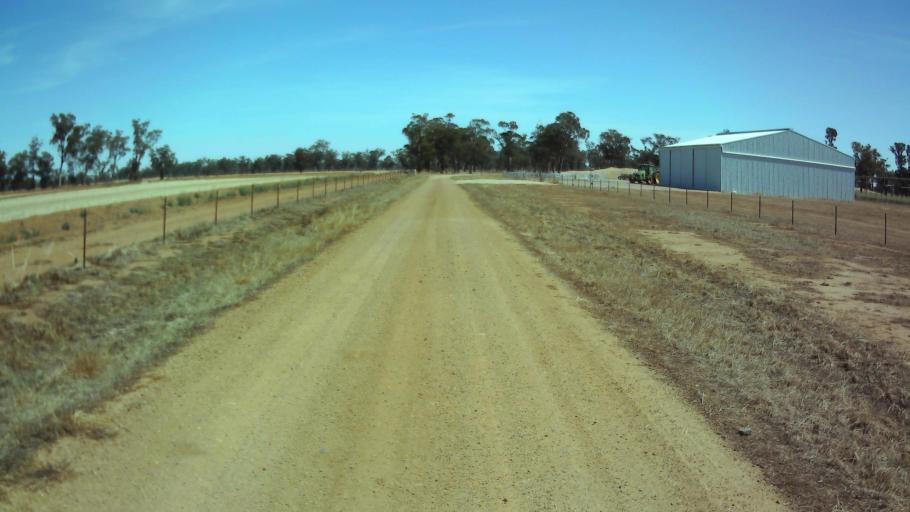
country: AU
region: New South Wales
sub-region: Weddin
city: Grenfell
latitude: -34.1165
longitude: 147.8152
